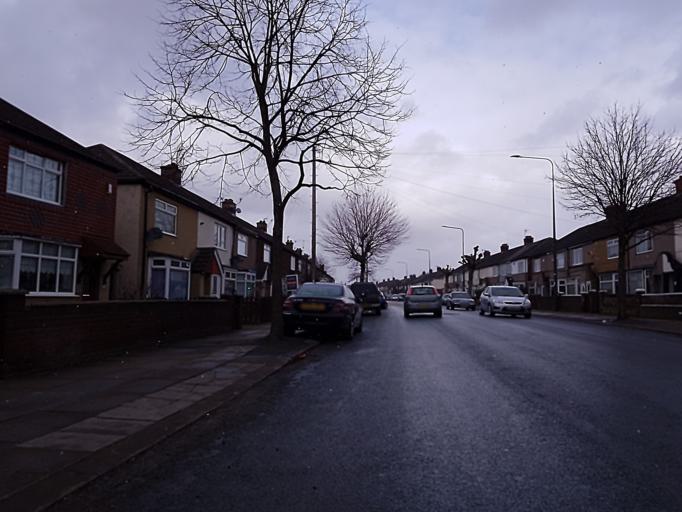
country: GB
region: England
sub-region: North East Lincolnshire
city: Grimbsy
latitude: 53.5689
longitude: -0.0998
